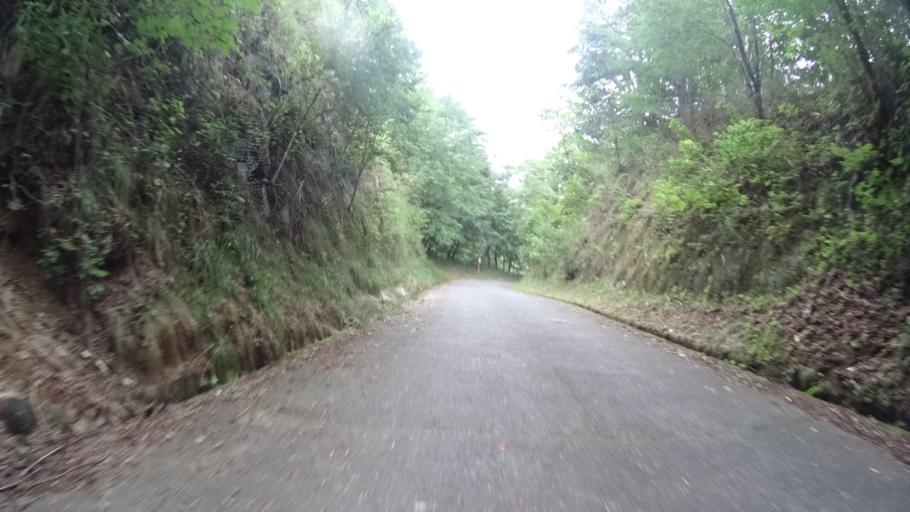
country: JP
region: Yamanashi
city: Kofu-shi
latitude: 35.8274
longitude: 138.5855
